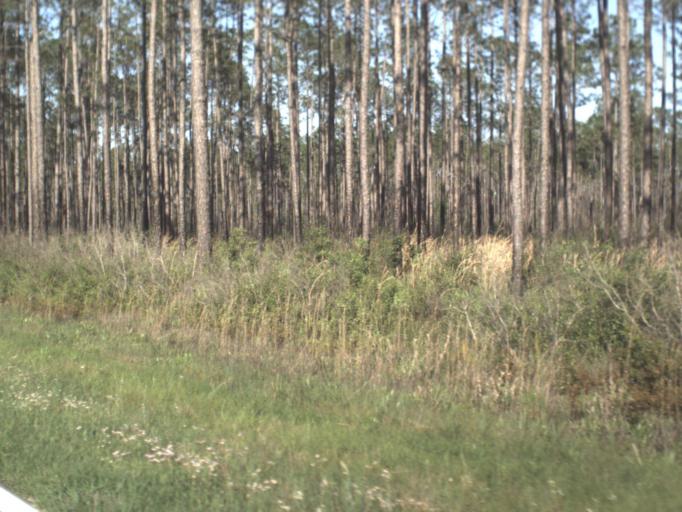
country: US
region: Florida
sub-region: Gulf County
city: Wewahitchka
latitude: 30.1483
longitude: -84.9719
